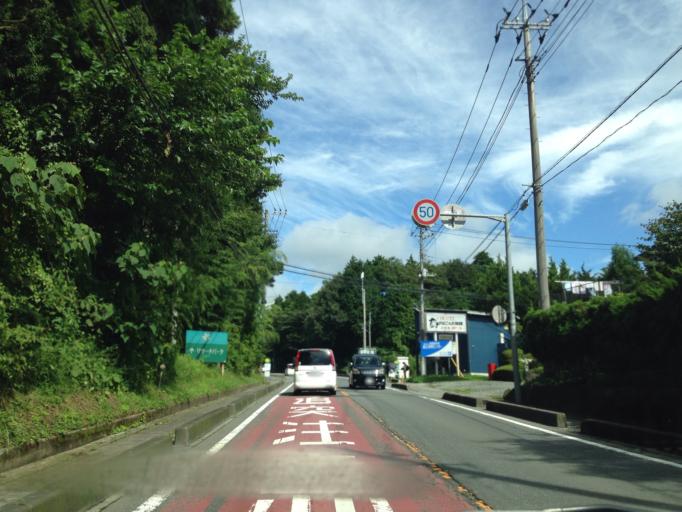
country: JP
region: Shizuoka
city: Gotemba
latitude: 35.3382
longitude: 138.8920
